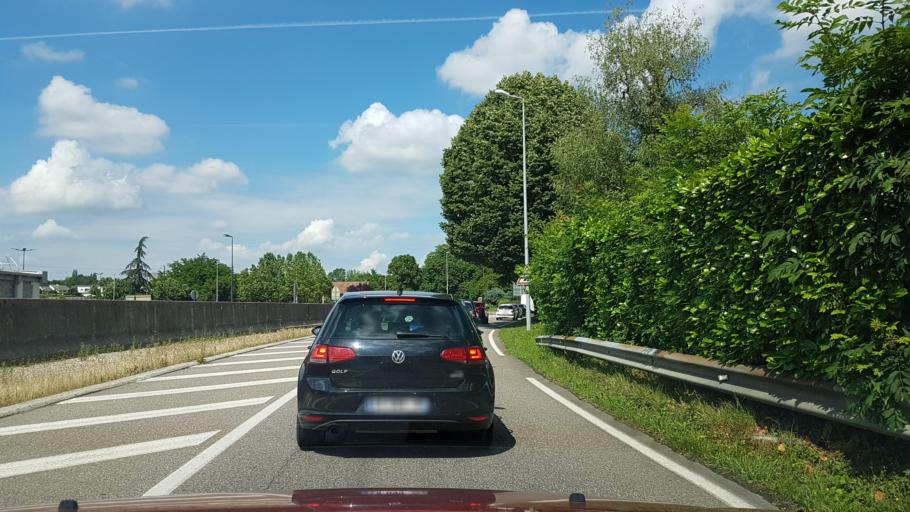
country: FR
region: Franche-Comte
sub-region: Departement du Jura
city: Perrigny
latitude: 46.6686
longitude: 5.5723
